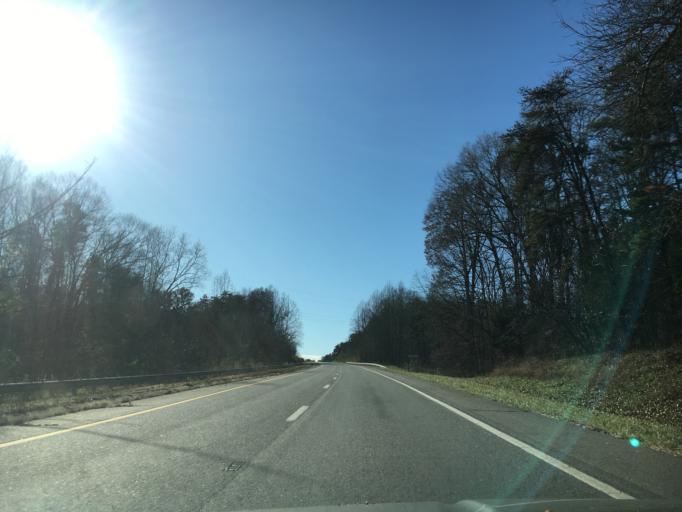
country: US
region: Virginia
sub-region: Henry County
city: Chatmoss
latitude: 36.6374
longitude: -79.8340
